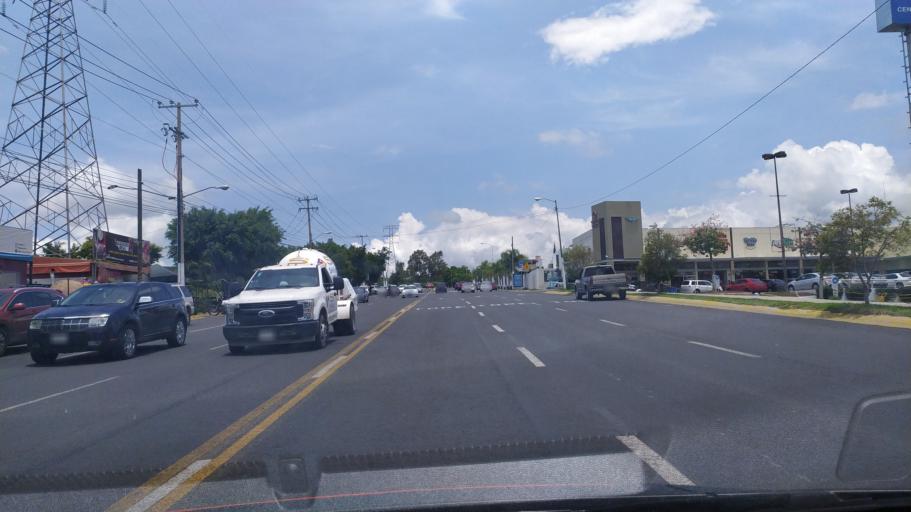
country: MX
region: Jalisco
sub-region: Zapopan
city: Zapopan
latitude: 20.7544
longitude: -103.3853
